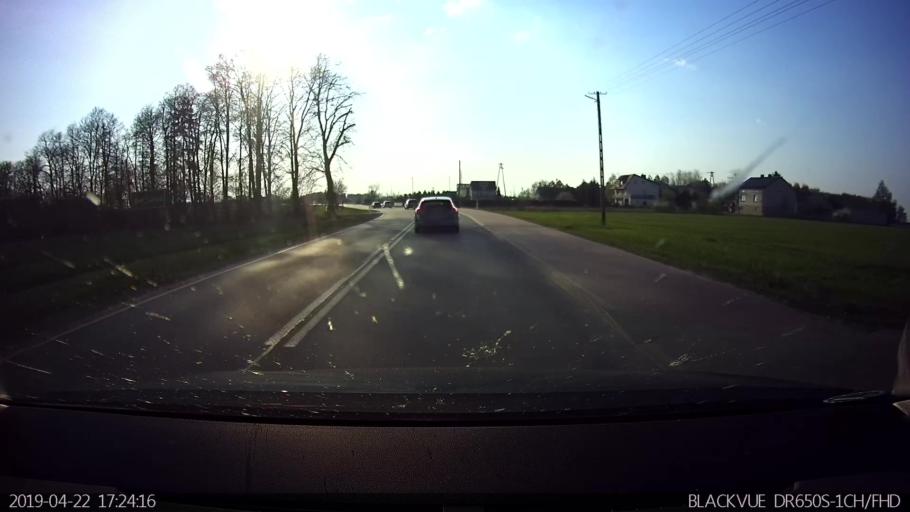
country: PL
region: Masovian Voivodeship
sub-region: Powiat sokolowski
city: Sokolow Podlaski
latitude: 52.3944
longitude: 22.3057
